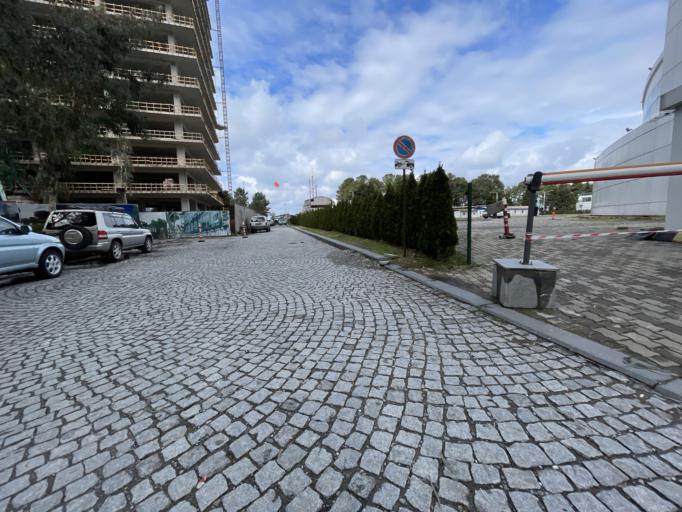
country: GE
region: Ajaria
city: Batumi
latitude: 41.6550
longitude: 41.6365
